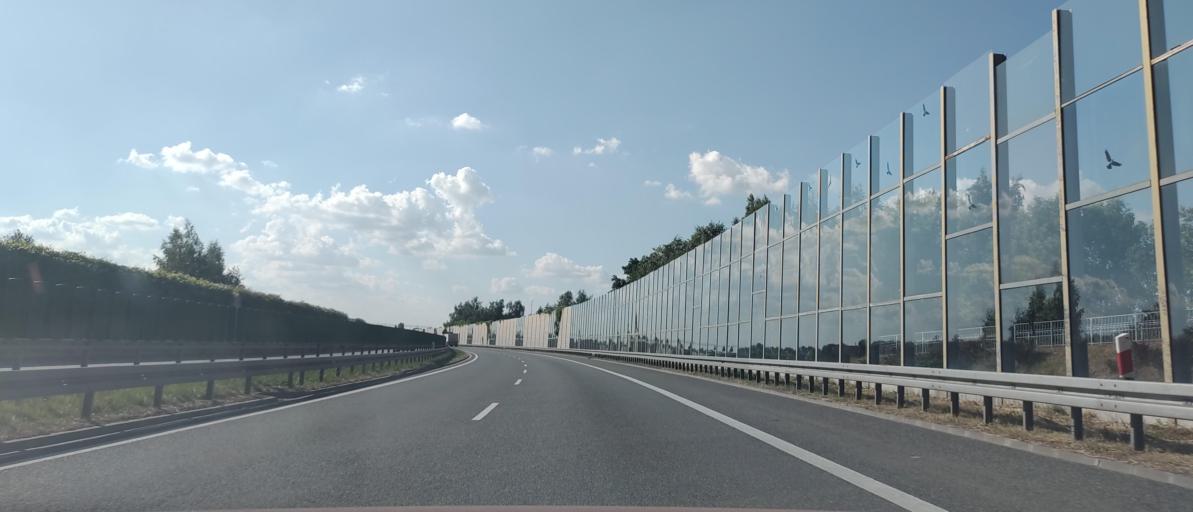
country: PL
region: Masovian Voivodeship
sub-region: Powiat grojecki
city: Grojec
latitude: 51.8545
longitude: 20.8707
